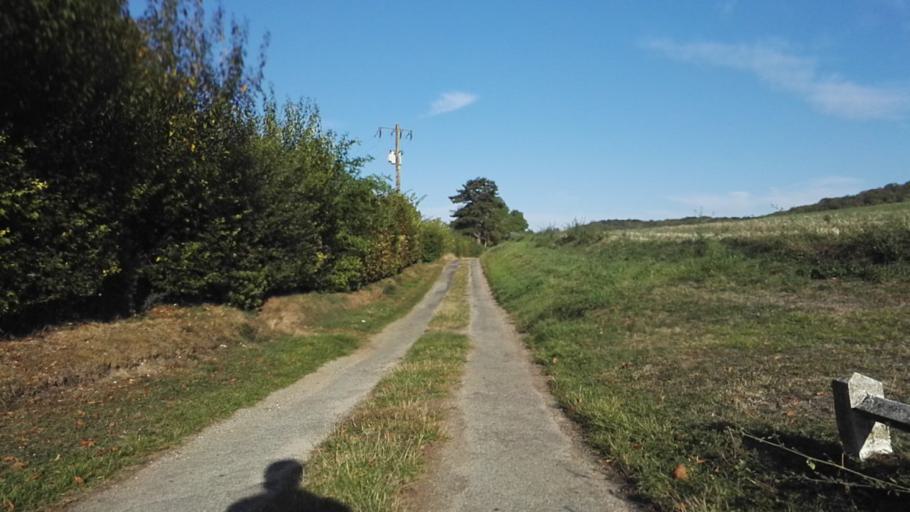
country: FR
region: Haute-Normandie
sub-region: Departement de l'Eure
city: Houlbec-Cocherel
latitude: 49.0529
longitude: 1.3395
